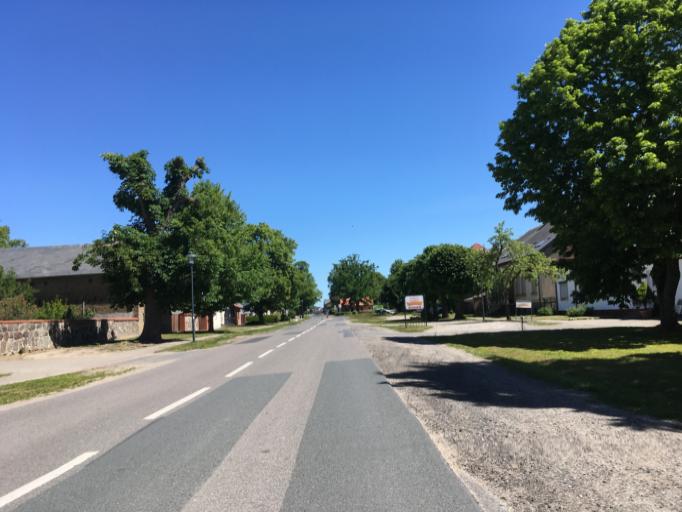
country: DE
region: Brandenburg
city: Zehdenick
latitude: 52.9298
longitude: 13.2584
